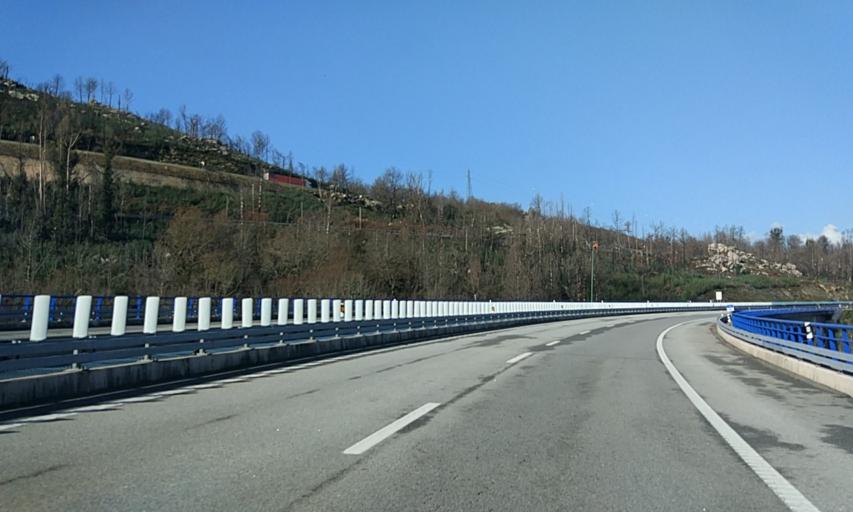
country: PT
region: Viseu
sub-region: Vouzela
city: Vouzela
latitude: 40.7010
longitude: -8.1068
